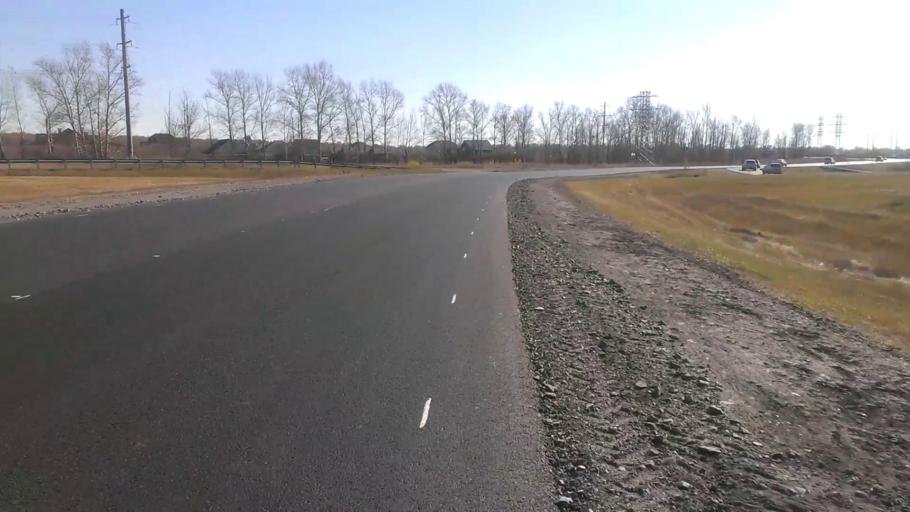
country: RU
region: Altai Krai
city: Sannikovo
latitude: 53.3399
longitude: 83.9378
